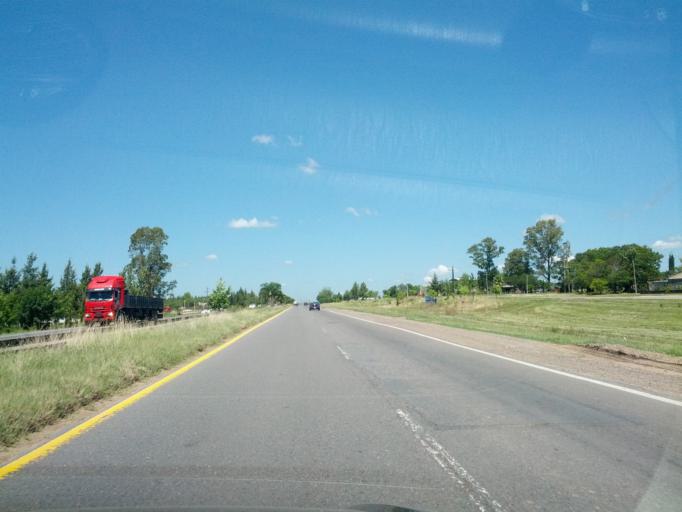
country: AR
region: Entre Rios
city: Gualeguaychu
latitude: -33.0572
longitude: -58.6257
